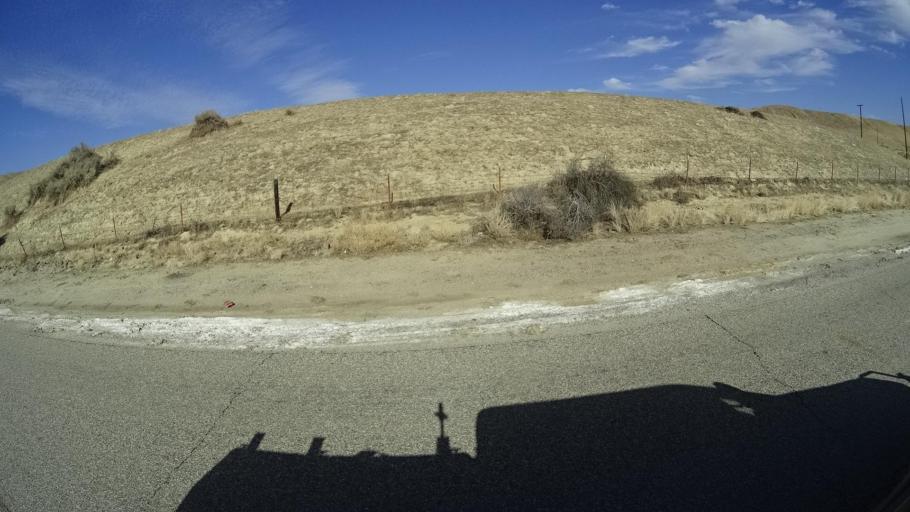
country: US
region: California
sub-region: Kern County
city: Oildale
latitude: 35.5267
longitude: -118.9380
